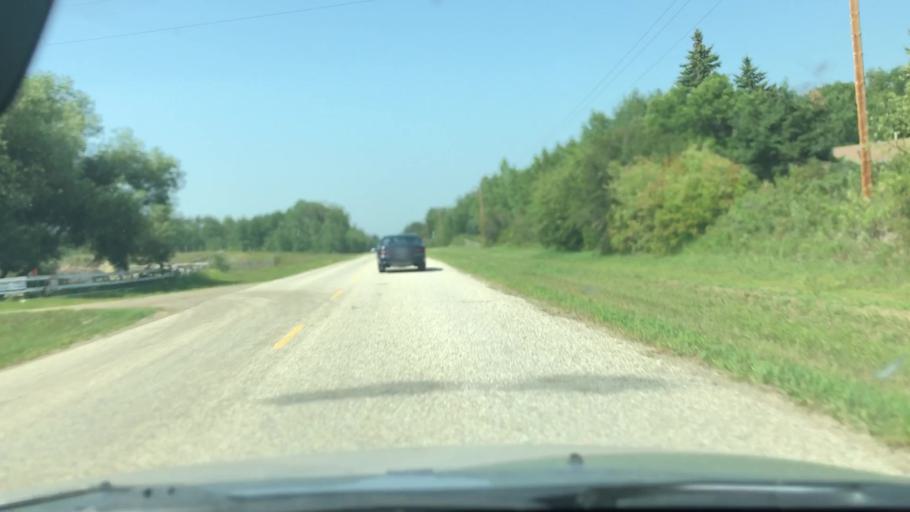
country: CA
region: Alberta
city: Devon
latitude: 53.4252
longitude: -113.7735
